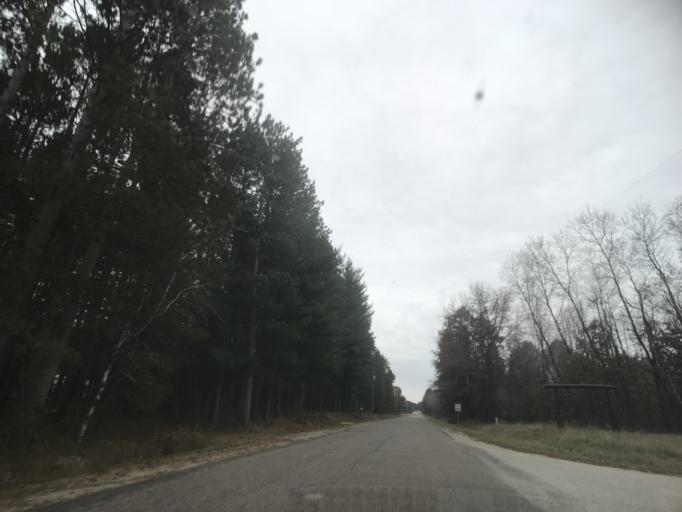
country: US
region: Wisconsin
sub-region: Oconto County
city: Gillett
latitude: 45.2807
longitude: -88.2570
